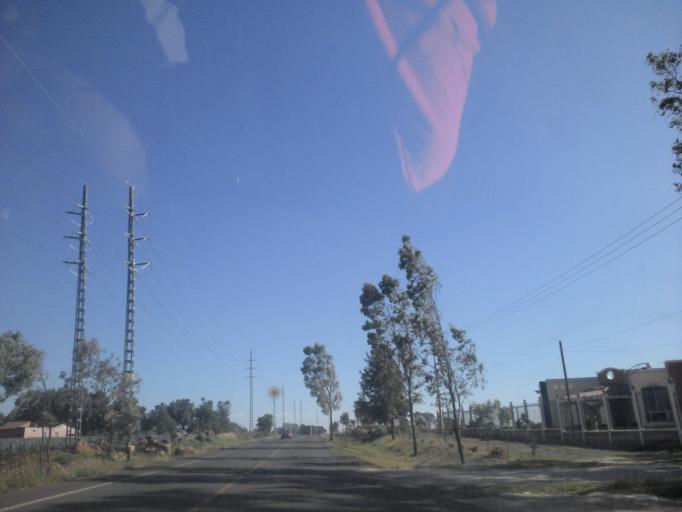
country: MX
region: Jalisco
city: Arandas
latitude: 20.7155
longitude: -102.3755
